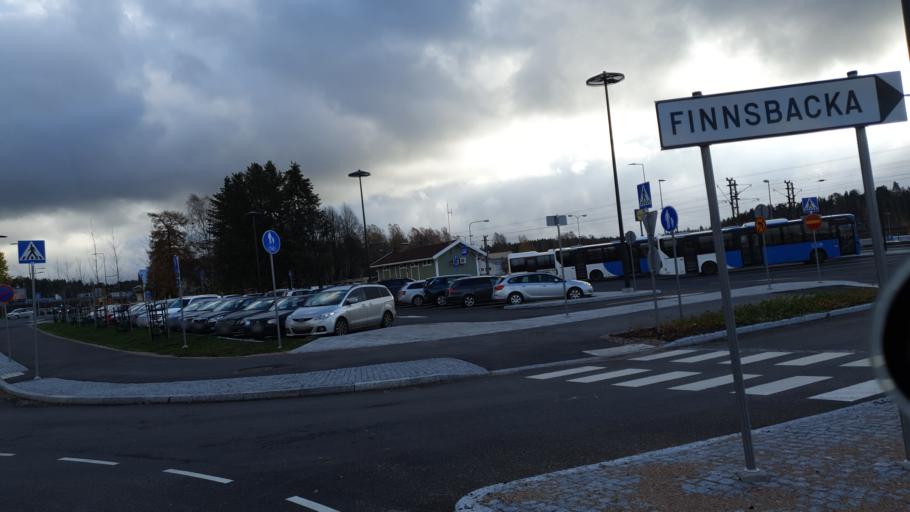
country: FI
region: Uusimaa
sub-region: Helsinki
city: Kirkkonummi
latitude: 60.1203
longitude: 24.4354
